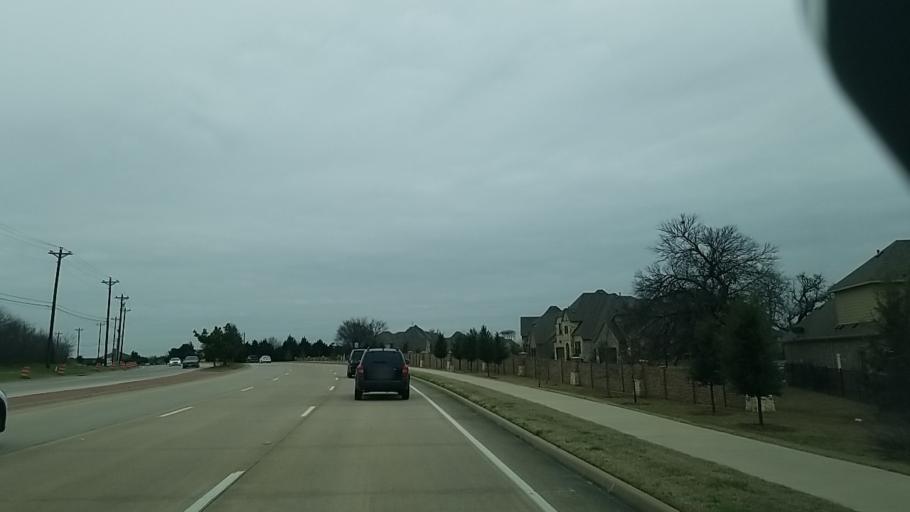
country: US
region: Texas
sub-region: Denton County
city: Flower Mound
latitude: 33.0017
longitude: -97.0700
